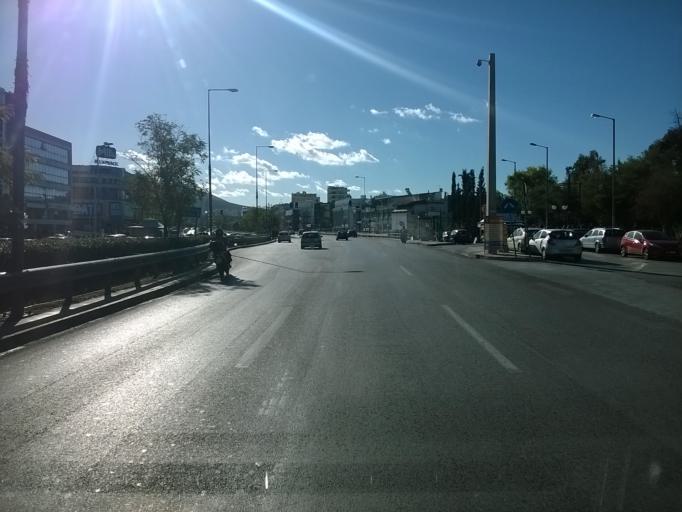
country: GR
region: Attica
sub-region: Nomarchia Athinas
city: Agios Dimitrios
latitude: 37.9390
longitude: 23.7410
